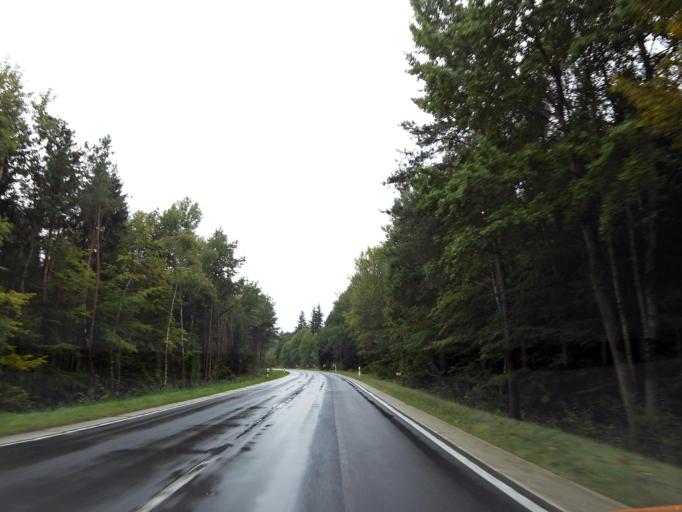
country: DE
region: Rheinland-Pfalz
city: Klosterkumbd
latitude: 50.0261
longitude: 7.5476
